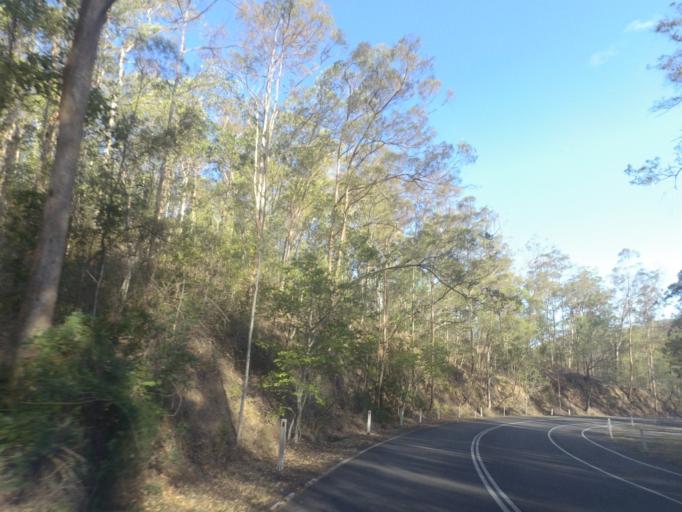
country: AU
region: Queensland
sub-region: Brisbane
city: Taringa
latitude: -27.4636
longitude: 152.9625
